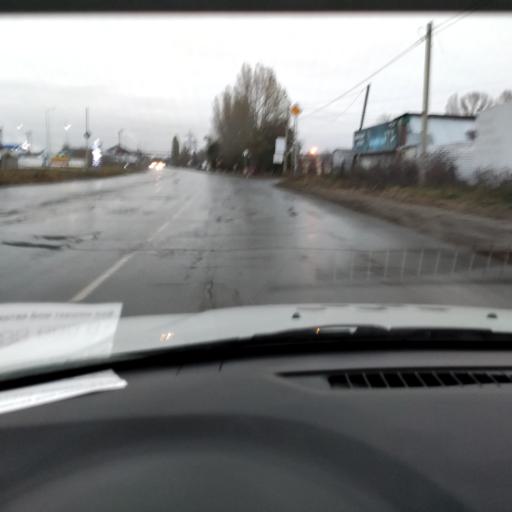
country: RU
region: Samara
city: Tol'yatti
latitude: 53.5217
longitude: 49.4692
